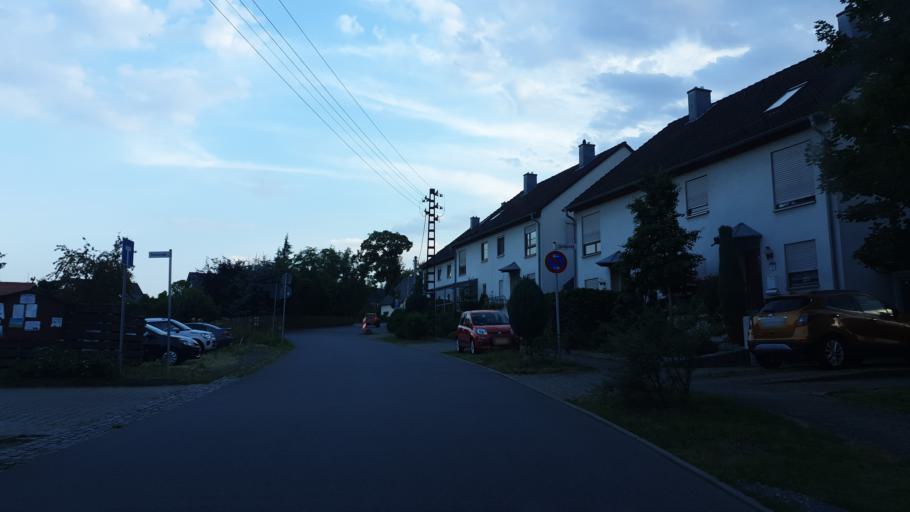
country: DE
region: Saxony
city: Kirchberg
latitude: 50.7930
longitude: 12.7858
